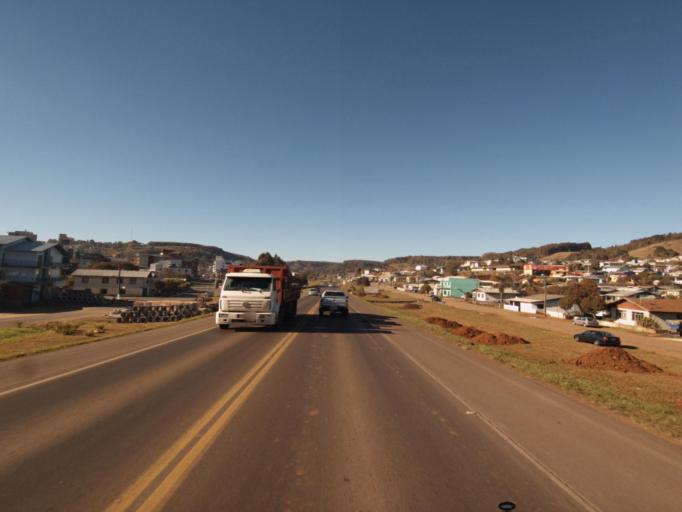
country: BR
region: Santa Catarina
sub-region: Concordia
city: Concordia
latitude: -26.8697
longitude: -52.0206
